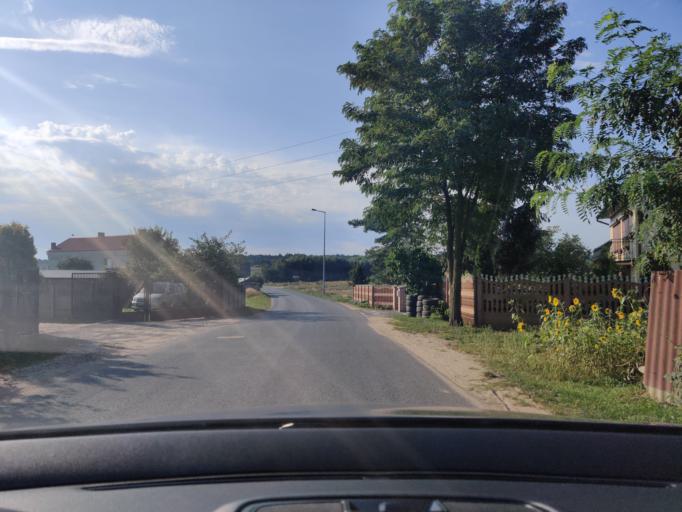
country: PL
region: Greater Poland Voivodeship
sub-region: Konin
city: Konin
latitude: 52.1882
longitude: 18.3229
